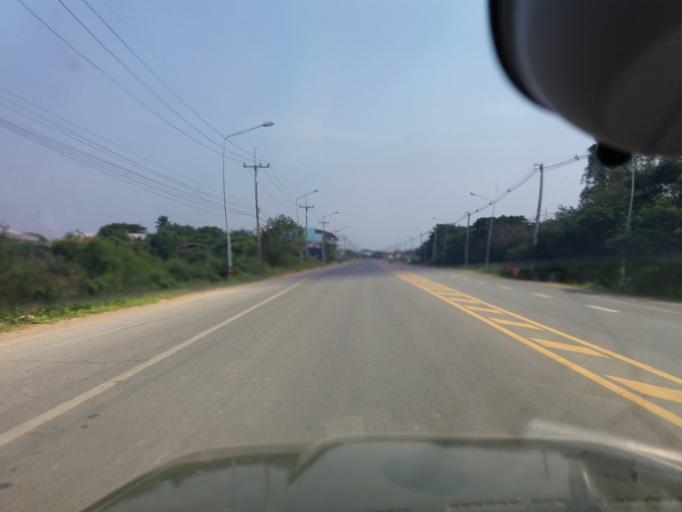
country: TH
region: Sing Buri
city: Sing Buri
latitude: 14.8860
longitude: 100.3738
